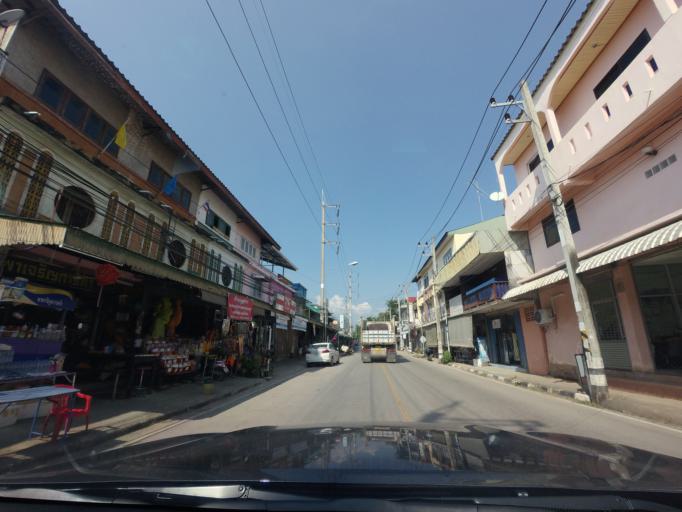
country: TH
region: Phitsanulok
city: Nakhon Thai
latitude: 17.1023
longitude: 100.8381
